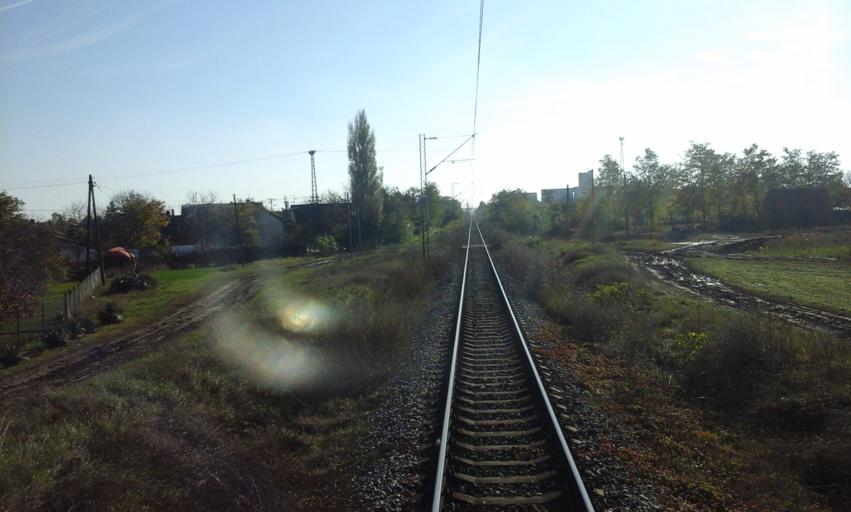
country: RS
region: Autonomna Pokrajina Vojvodina
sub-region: Severnobacki Okrug
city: Backa Topola
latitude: 45.8269
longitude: 19.6509
